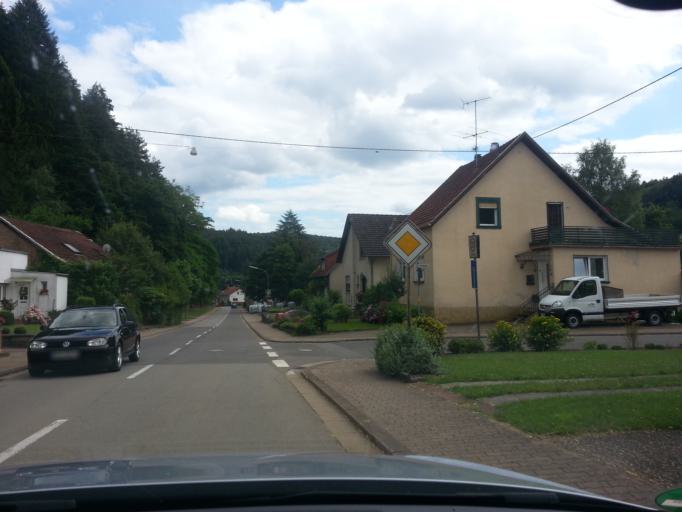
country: DE
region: Saarland
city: Beckingen
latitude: 49.4314
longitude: 6.7268
